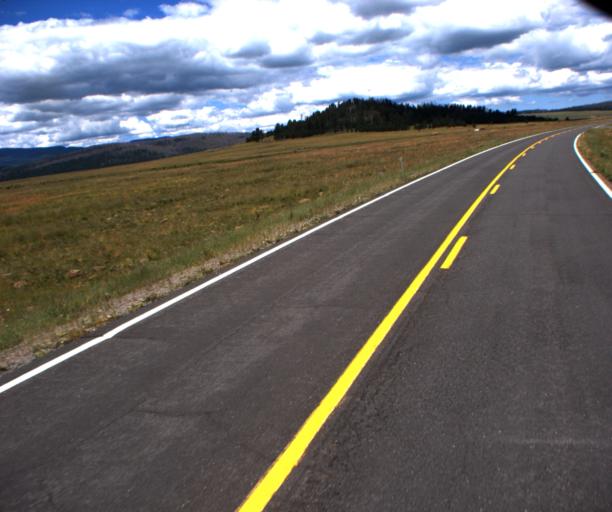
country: US
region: Arizona
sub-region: Apache County
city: Eagar
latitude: 33.8968
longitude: -109.4117
